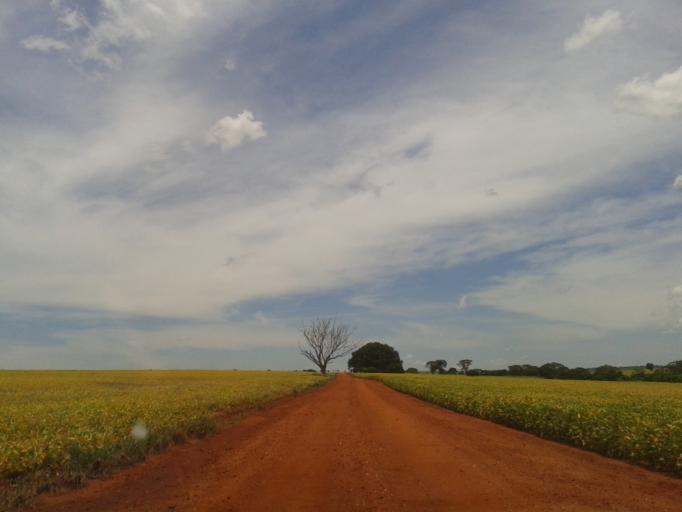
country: BR
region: Minas Gerais
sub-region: Capinopolis
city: Capinopolis
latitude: -18.6937
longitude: -49.7096
